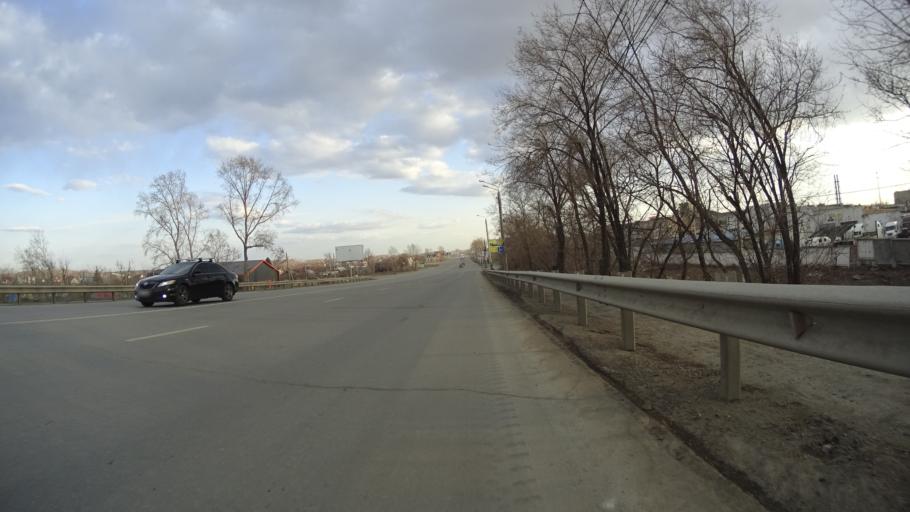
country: RU
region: Chelyabinsk
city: Novosineglazovskiy
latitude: 55.0999
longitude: 61.3876
